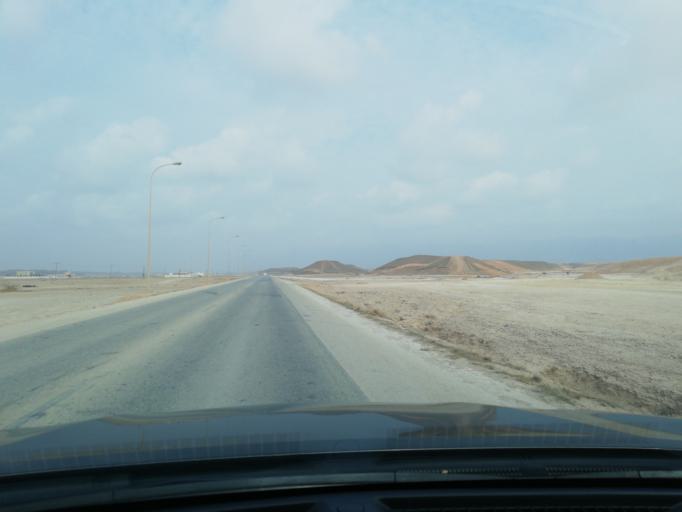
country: OM
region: Zufar
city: Salalah
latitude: 16.9476
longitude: 53.9440
